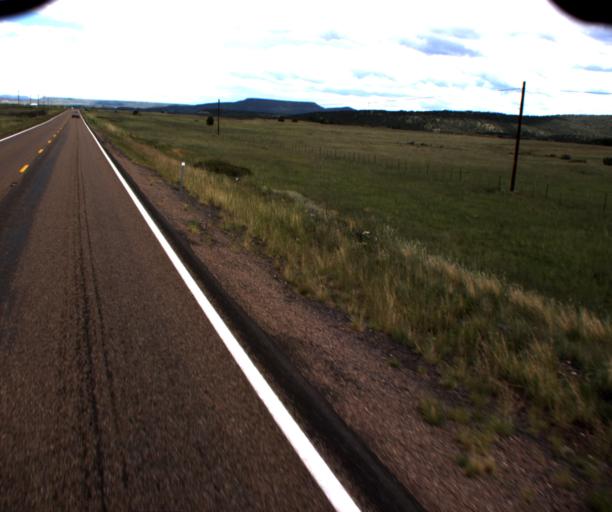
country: US
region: Arizona
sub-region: Apache County
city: Eagar
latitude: 34.1018
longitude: -109.3768
